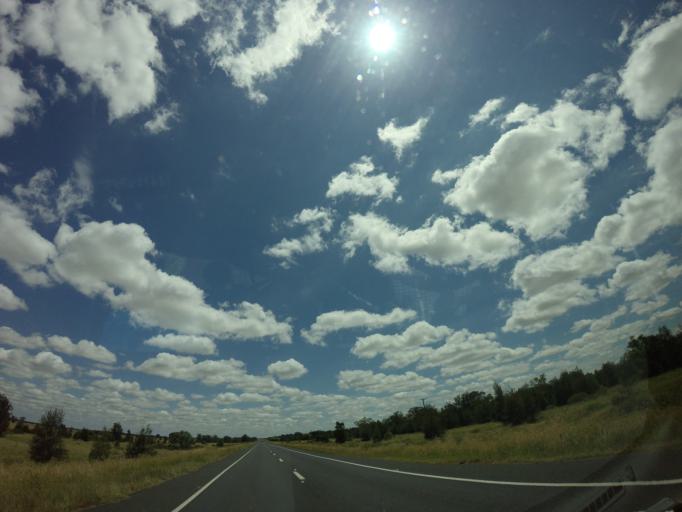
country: AU
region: New South Wales
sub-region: Moree Plains
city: Moree
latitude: -29.1414
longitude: 150.0210
